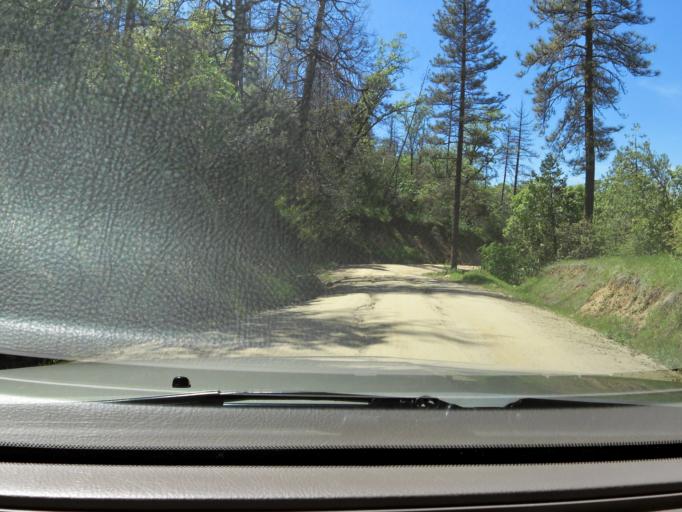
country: US
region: California
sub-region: Madera County
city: Oakhurst
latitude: 37.2848
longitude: -119.6221
